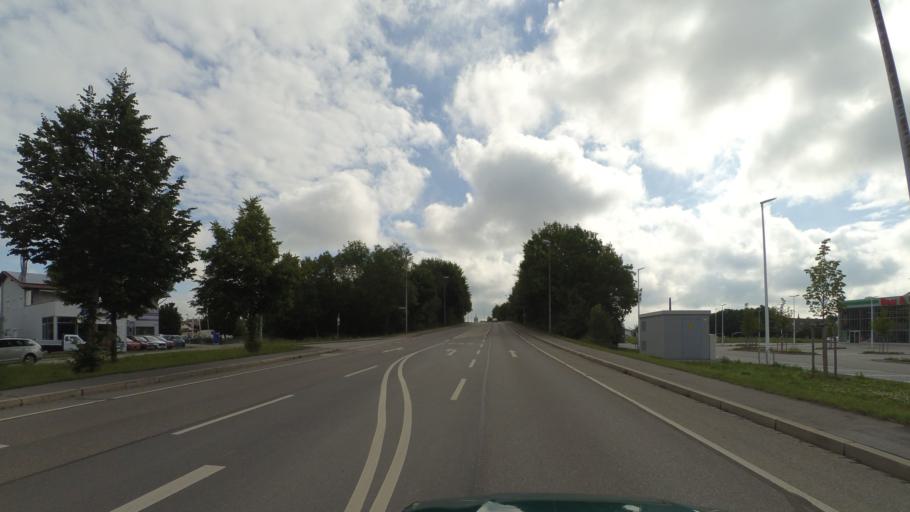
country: DE
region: Bavaria
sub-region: Lower Bavaria
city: Straubing
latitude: 48.8768
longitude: 12.5555
